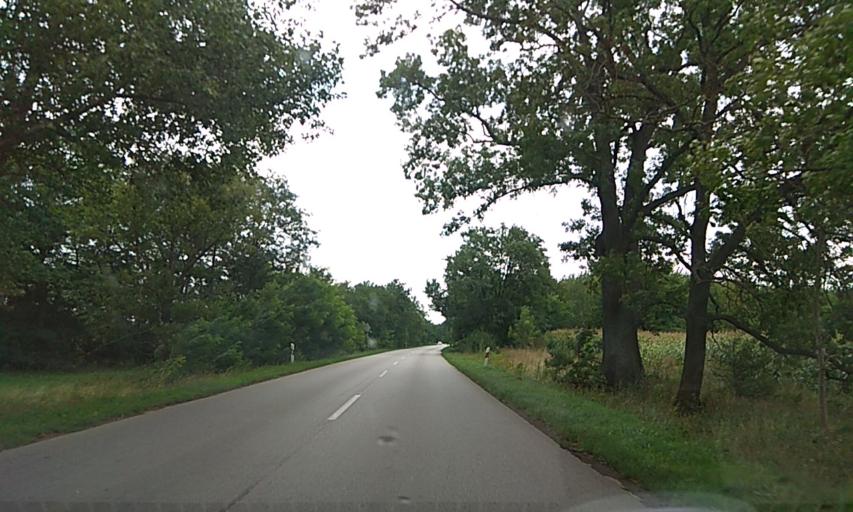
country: HU
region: Szabolcs-Szatmar-Bereg
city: Buj
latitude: 48.0614
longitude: 21.6512
